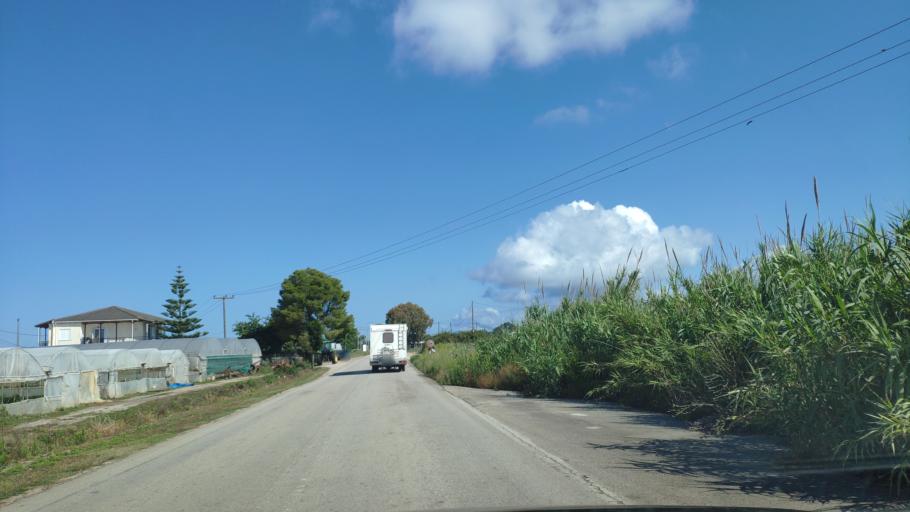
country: GR
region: Epirus
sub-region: Nomos Prevezis
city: Preveza
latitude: 38.9338
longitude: 20.7714
